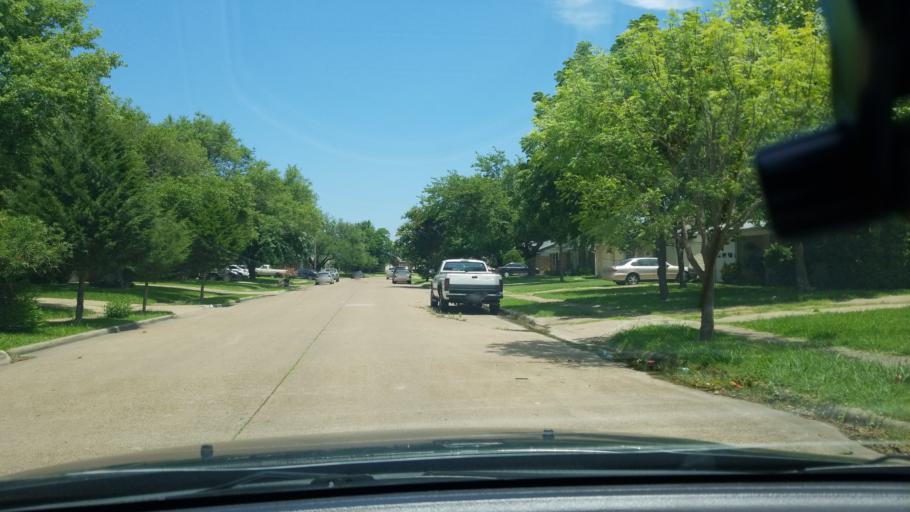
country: US
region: Texas
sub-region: Dallas County
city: Mesquite
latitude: 32.8055
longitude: -96.6573
